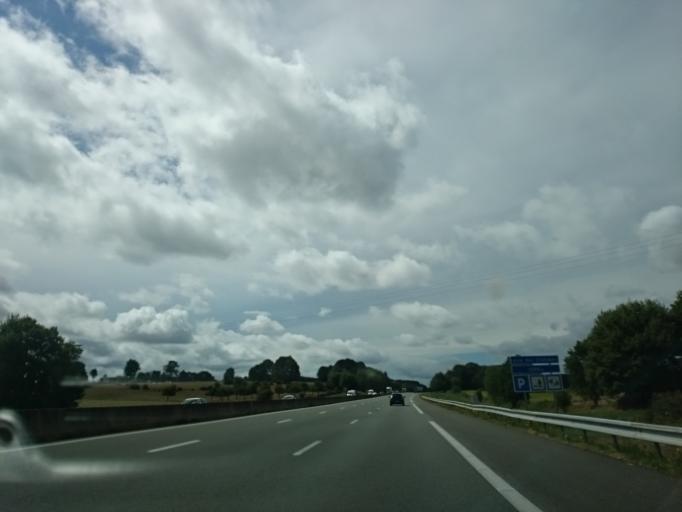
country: FR
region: Centre
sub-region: Departement d'Eure-et-Loir
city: Authon-du-Perche
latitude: 48.2192
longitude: 0.9587
